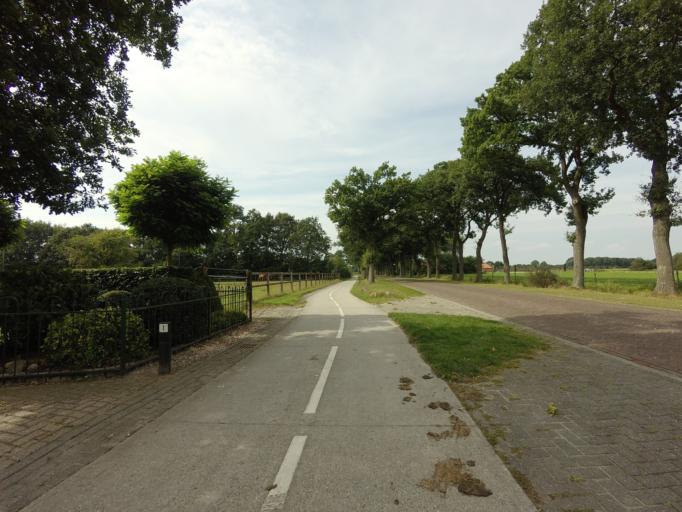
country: NL
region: Drenthe
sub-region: Gemeente Westerveld
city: Dwingeloo
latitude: 52.9085
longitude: 6.2846
